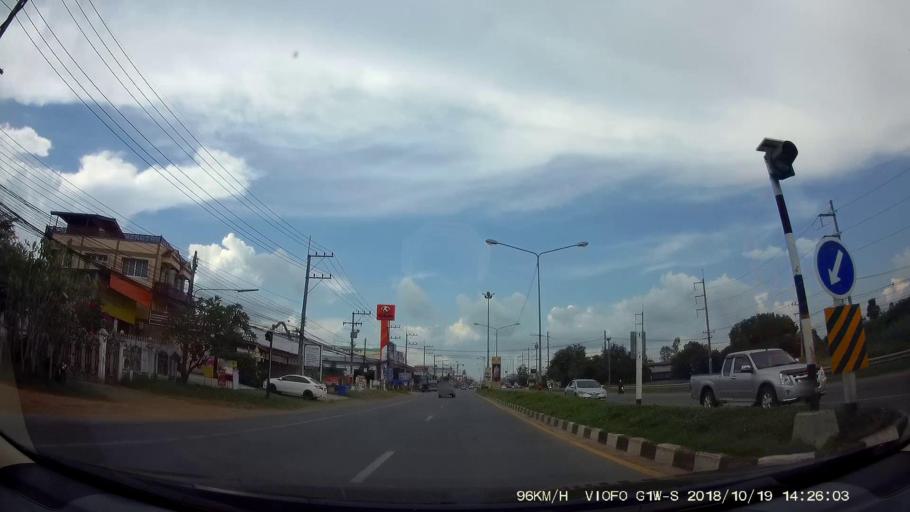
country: TH
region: Chaiyaphum
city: Kaeng Khro
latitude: 16.1023
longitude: 102.2612
